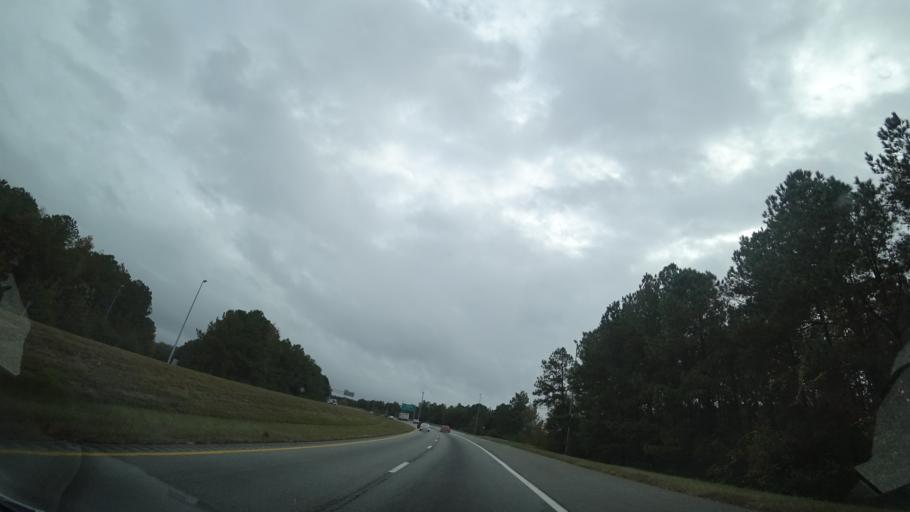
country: US
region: Virginia
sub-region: City of Portsmouth
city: Portsmouth Heights
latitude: 36.7889
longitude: -76.4256
